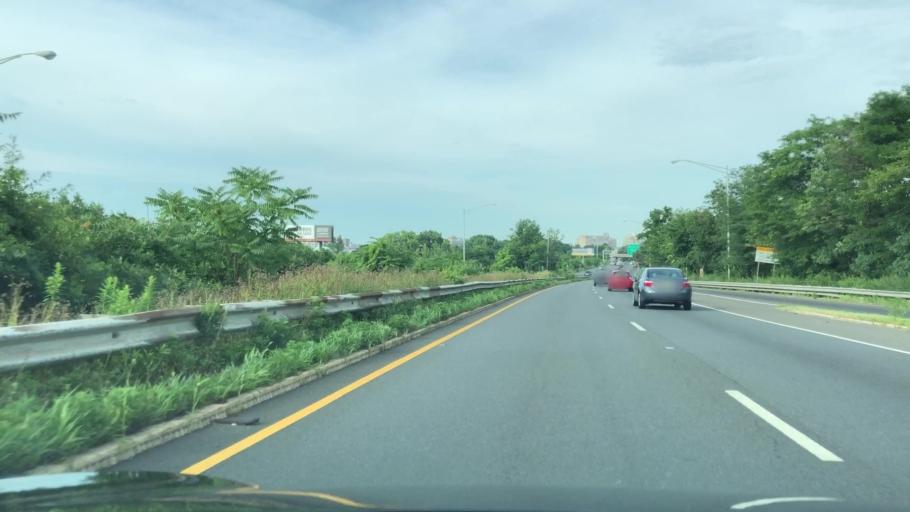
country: US
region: New Jersey
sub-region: Mercer County
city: Trenton
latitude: 40.2335
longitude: -74.7496
